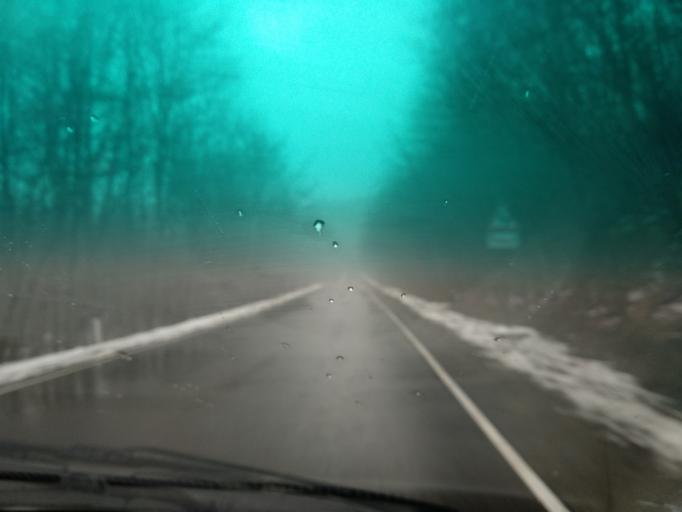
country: RU
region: Krasnodarskiy
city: Khadyzhensk
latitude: 44.2656
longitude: 39.3513
